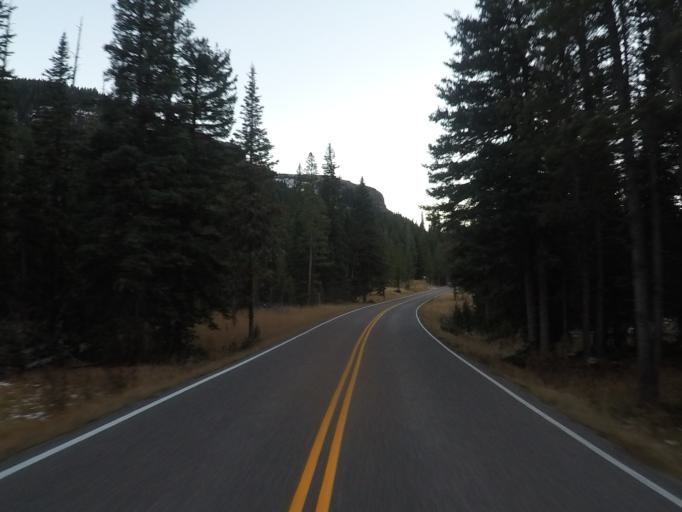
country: US
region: Montana
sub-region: Stillwater County
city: Absarokee
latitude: 44.9884
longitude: -110.0563
